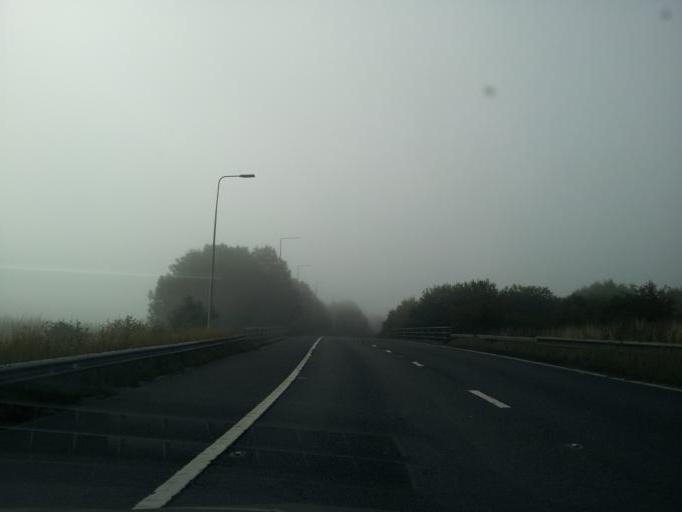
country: GB
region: England
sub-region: Borough of Rochdale
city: Rochdale
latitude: 53.5859
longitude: -2.1566
